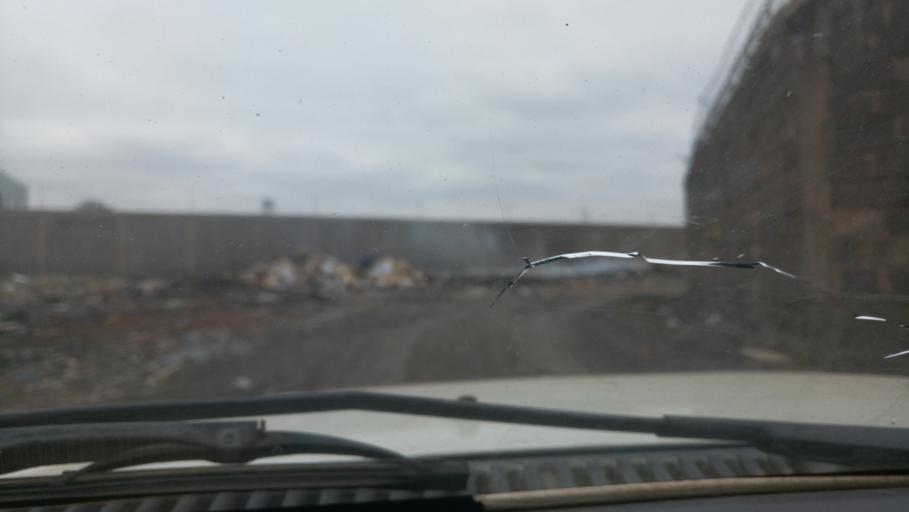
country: KE
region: Nairobi Area
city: Pumwani
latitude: -1.3371
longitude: 36.8691
